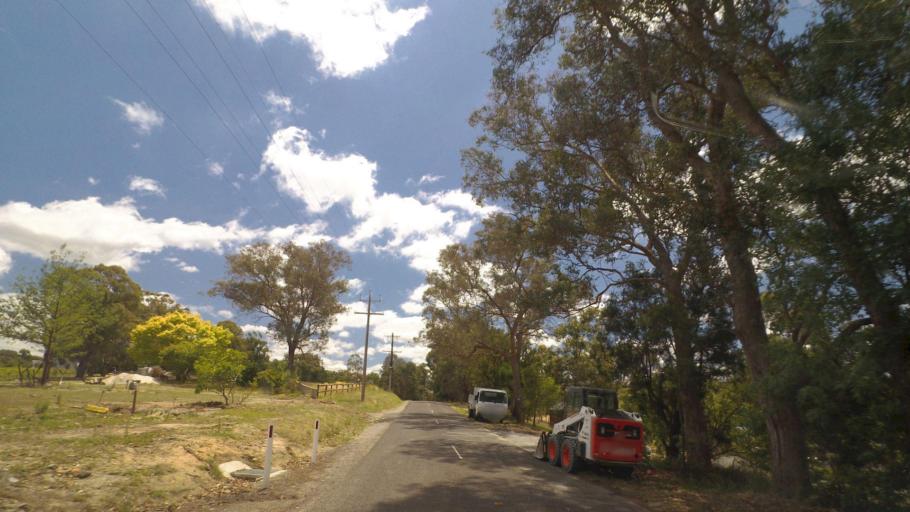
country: AU
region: Victoria
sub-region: Yarra Ranges
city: Chirnside Park
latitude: -37.7277
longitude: 145.2730
